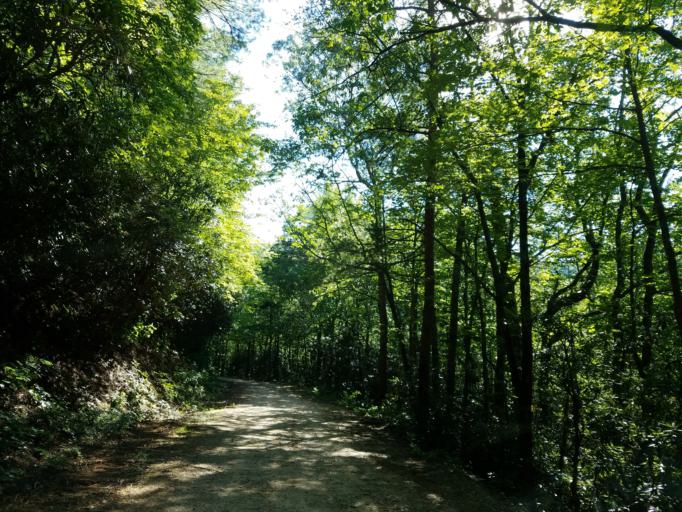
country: US
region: Georgia
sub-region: Dawson County
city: Dawsonville
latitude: 34.5874
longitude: -84.1986
